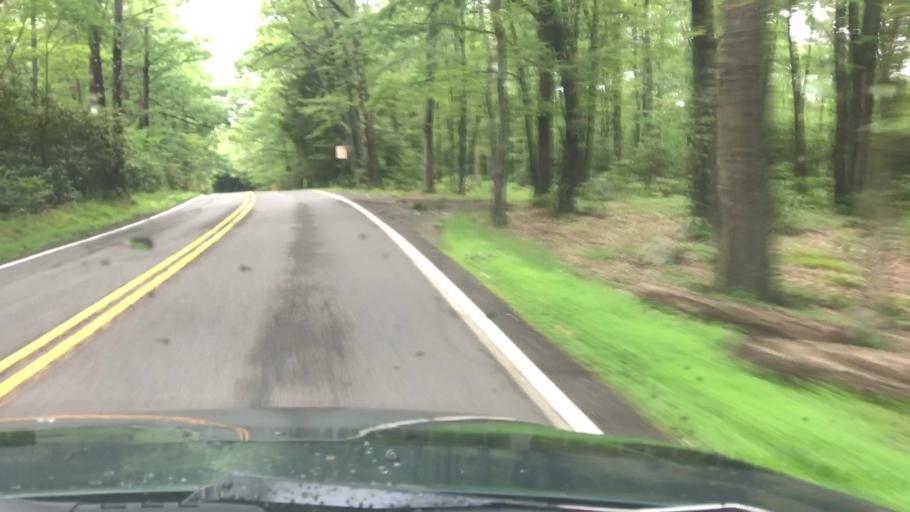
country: US
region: Pennsylvania
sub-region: Monroe County
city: Mountainhome
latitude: 41.3022
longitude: -75.2124
